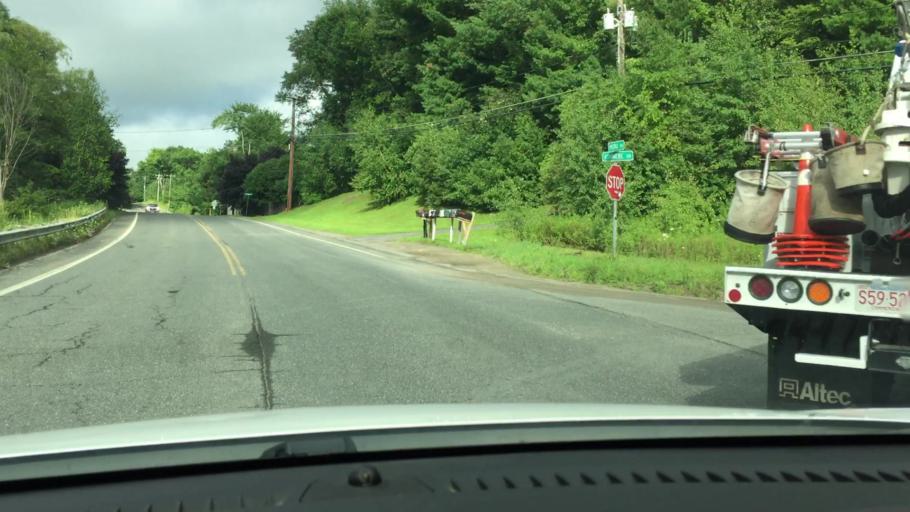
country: US
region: Massachusetts
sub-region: Berkshire County
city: Hinsdale
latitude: 42.4458
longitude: -73.0806
